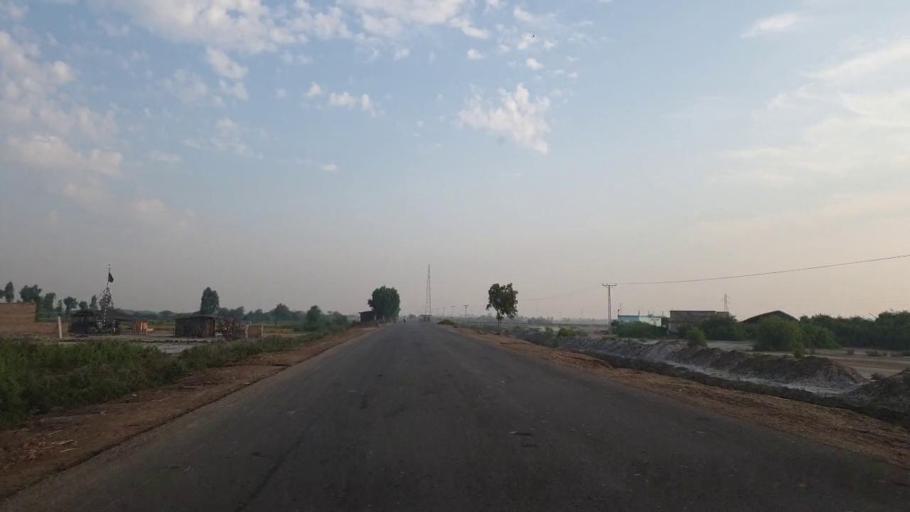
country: PK
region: Sindh
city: Badin
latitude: 24.6933
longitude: 68.9181
